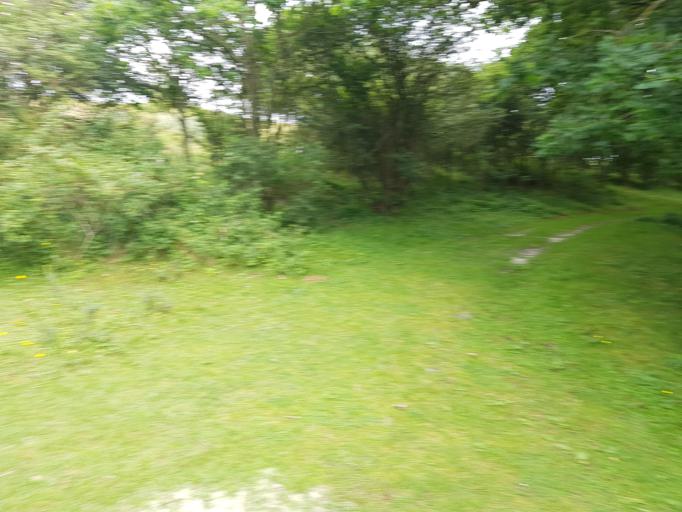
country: NL
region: North Holland
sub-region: Gemeente Bergen
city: Egmond aan Zee
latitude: 52.6476
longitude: 4.6372
